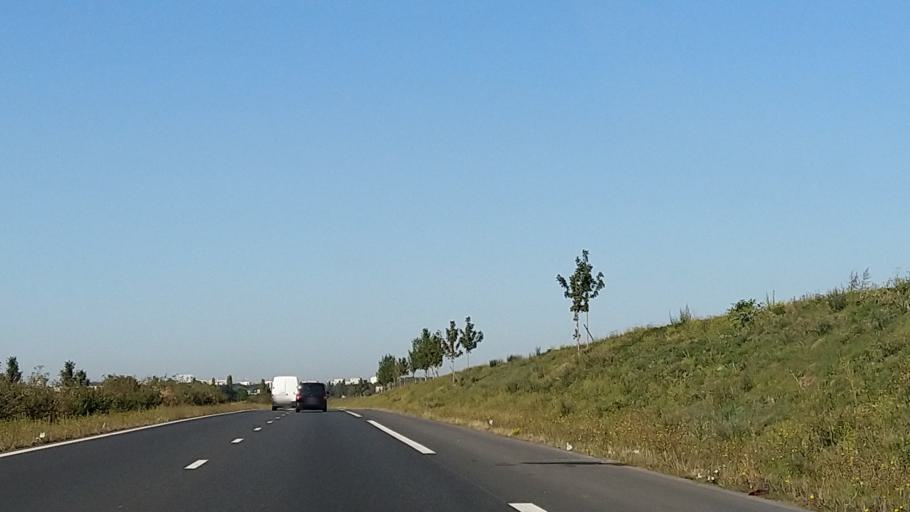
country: FR
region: Ile-de-France
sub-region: Departement du Val-d'Oise
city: Gonesse
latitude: 48.9780
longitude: 2.4466
